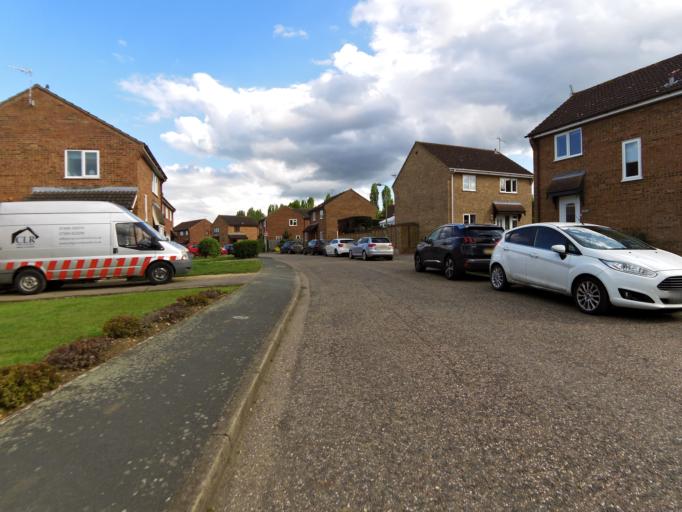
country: GB
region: England
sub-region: Suffolk
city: Stowmarket
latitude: 52.1948
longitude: 0.9777
